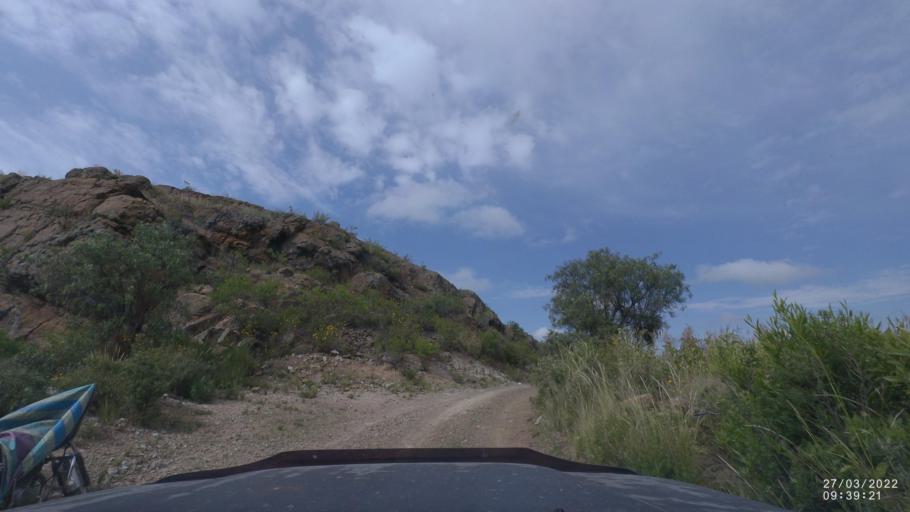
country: BO
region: Cochabamba
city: Cliza
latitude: -17.7497
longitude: -65.8976
